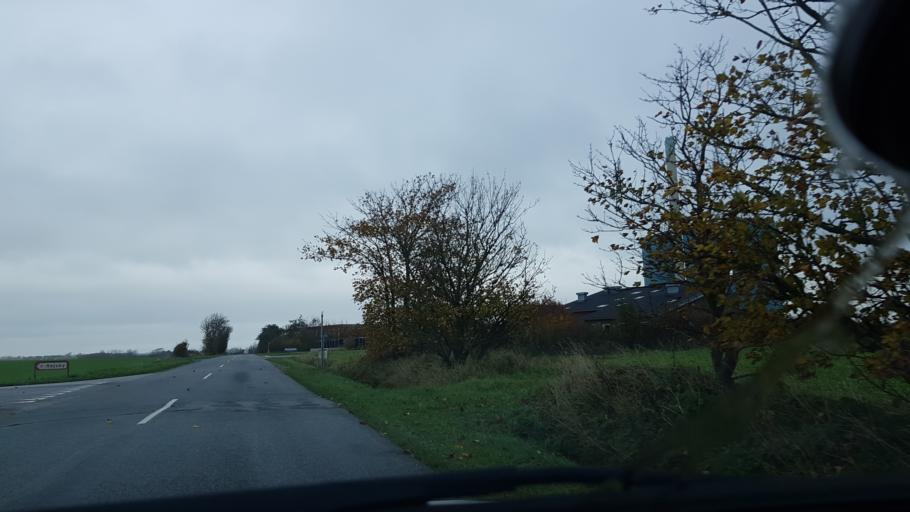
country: DK
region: South Denmark
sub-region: Tonder Kommune
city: Sherrebek
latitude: 55.2211
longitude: 8.8323
